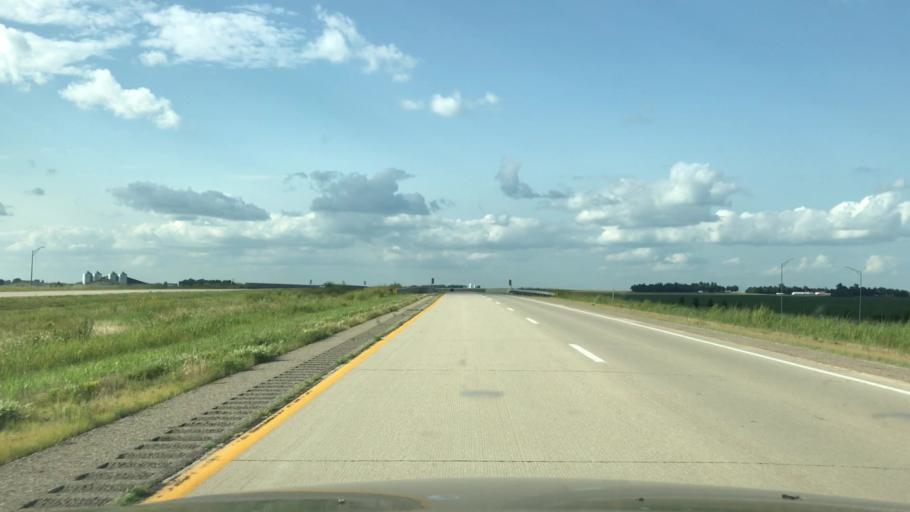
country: US
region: Iowa
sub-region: Osceola County
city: Sibley
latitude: 43.4311
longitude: -95.7136
